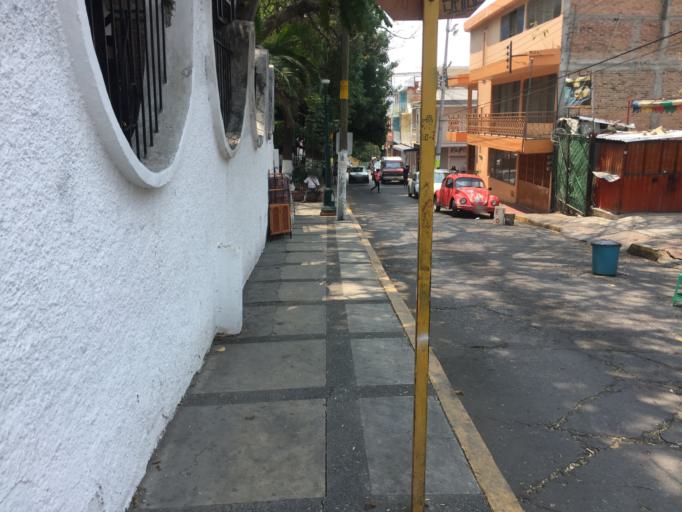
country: MX
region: Guerrero
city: Chilpancingo de los Bravos
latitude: 17.5551
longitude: -99.4989
